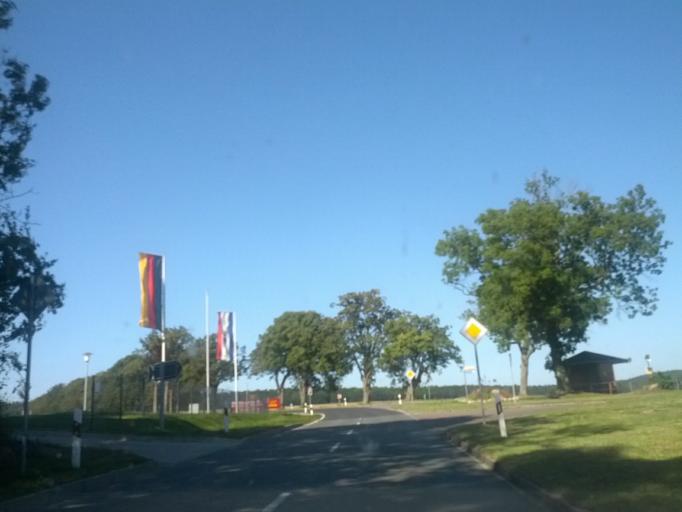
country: DE
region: Mecklenburg-Vorpommern
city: Ostseebad Gohren
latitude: 54.3320
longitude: 13.7050
